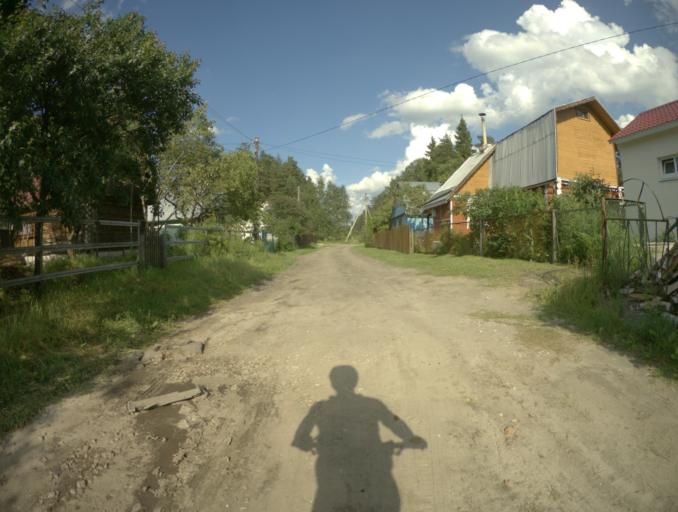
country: RU
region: Vladimir
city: Kommunar
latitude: 56.0375
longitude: 40.4595
